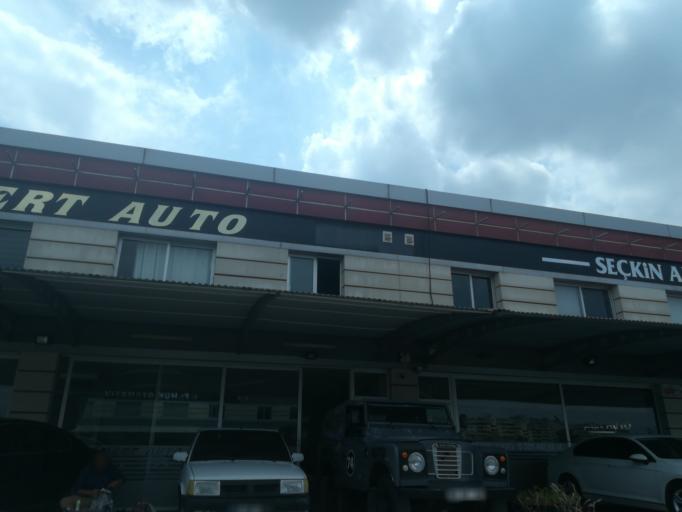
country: TR
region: Adana
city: Seyhan
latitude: 36.9994
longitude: 35.2431
